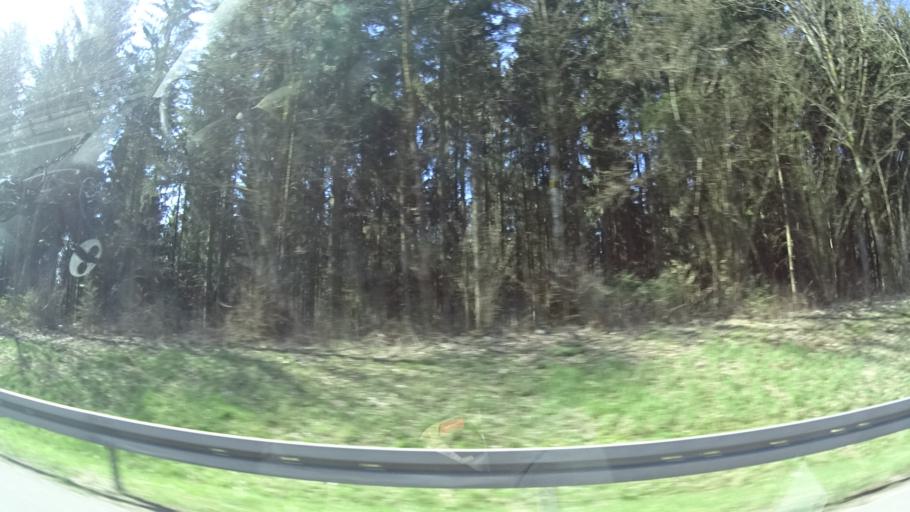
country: DE
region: Bavaria
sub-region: Regierungsbezirk Mittelfranken
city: Alfeld
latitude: 49.4109
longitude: 11.5279
